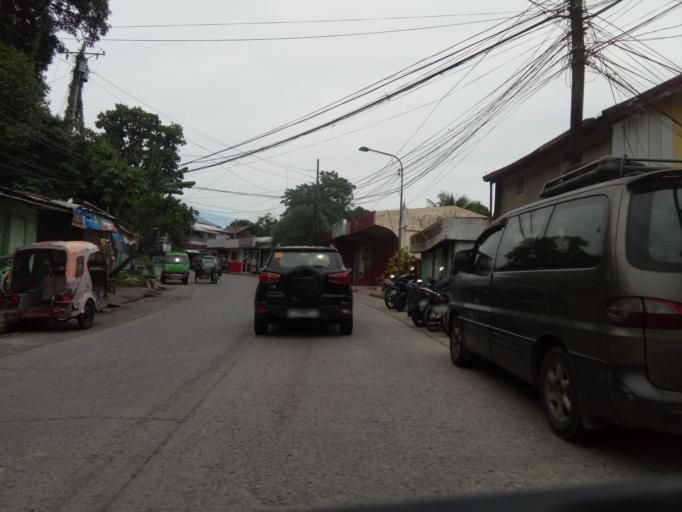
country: PH
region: Caraga
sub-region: Province of Surigao del Norte
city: Surigao
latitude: 9.7831
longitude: 125.4911
